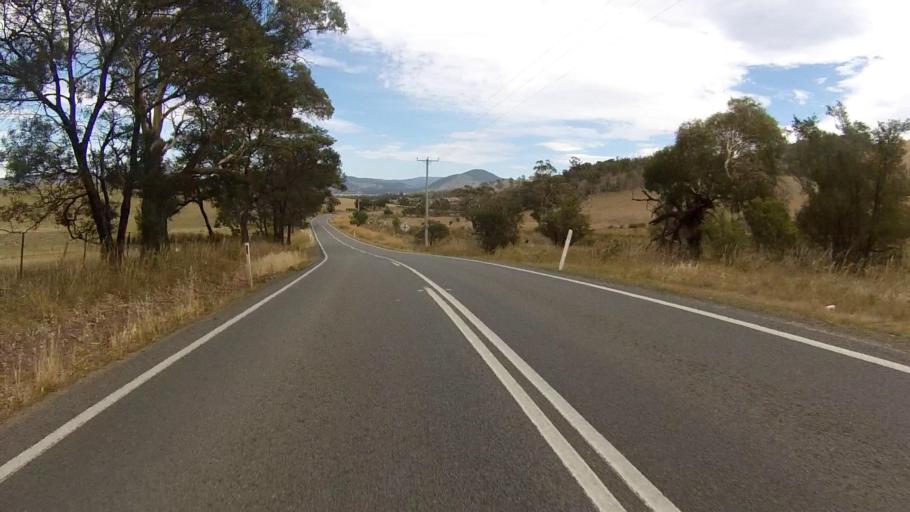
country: AU
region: Tasmania
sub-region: Sorell
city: Sorell
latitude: -42.7013
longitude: 147.4887
